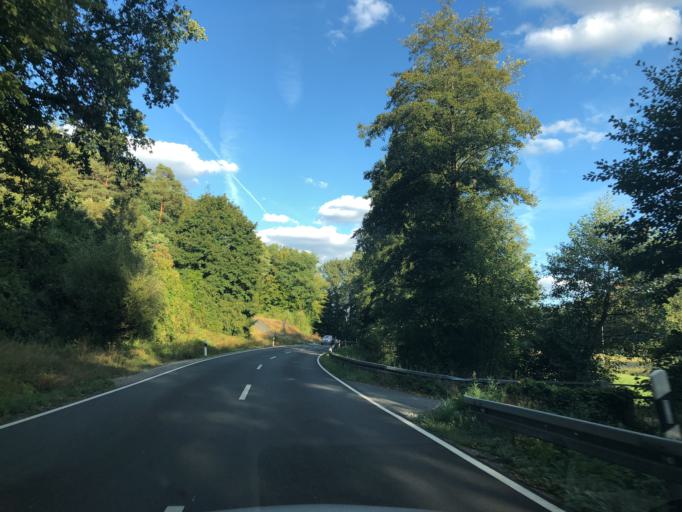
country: DE
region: Bavaria
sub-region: Upper Franconia
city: Burgwindheim
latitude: 49.8334
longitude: 10.5491
